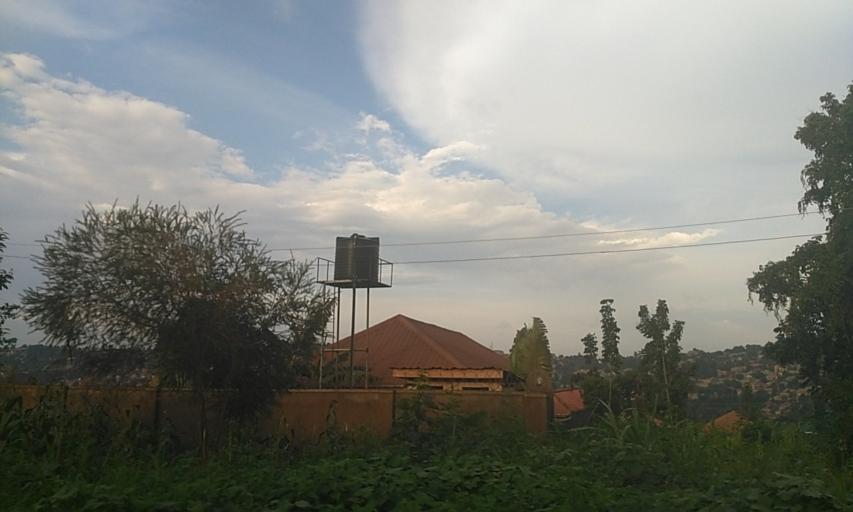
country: UG
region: Central Region
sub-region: Wakiso District
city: Kajansi
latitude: 0.2535
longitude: 32.5352
